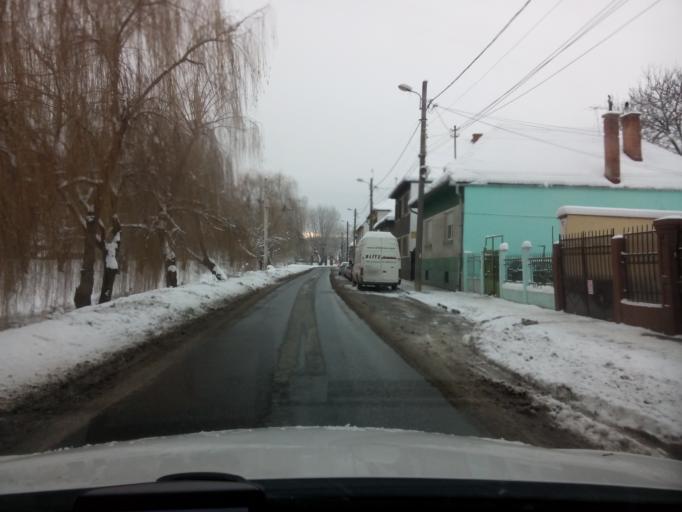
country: RO
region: Sibiu
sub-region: Municipiul Sibiu
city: Sibiu
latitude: 45.7986
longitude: 24.1427
